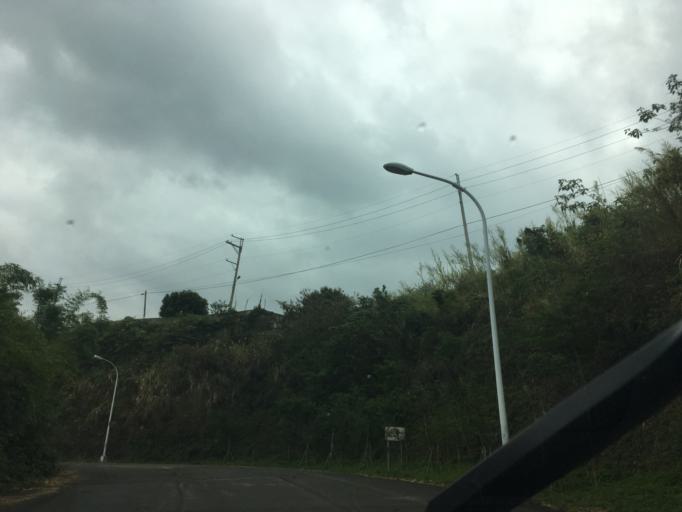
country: TW
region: Taiwan
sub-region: Taichung City
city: Taichung
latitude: 24.0638
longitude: 120.7203
